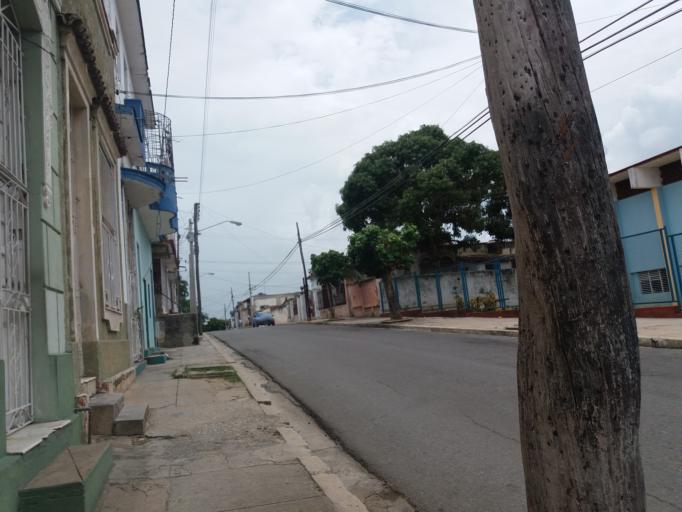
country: CU
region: Cienfuegos
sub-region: Municipio de Cienfuegos
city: Cienfuegos
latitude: 22.1473
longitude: -80.4440
